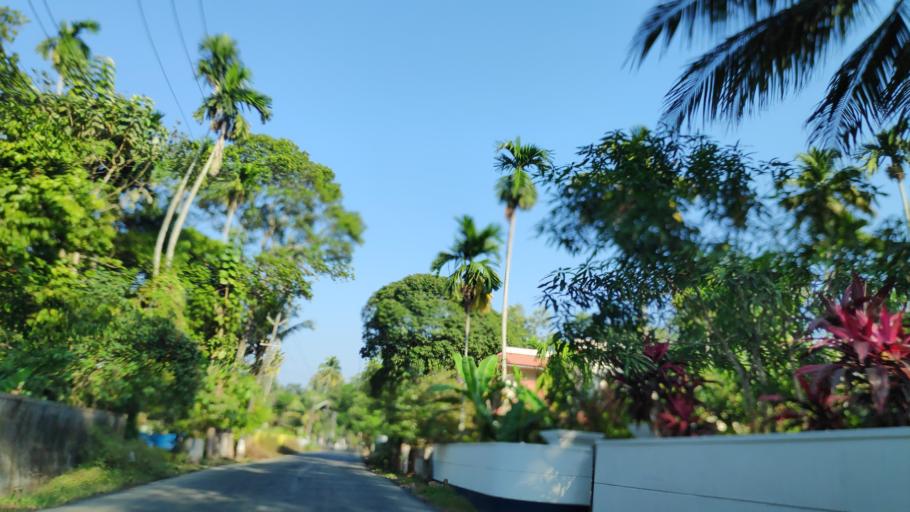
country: IN
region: Kerala
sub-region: Alappuzha
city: Alleppey
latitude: 9.5700
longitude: 76.3137
